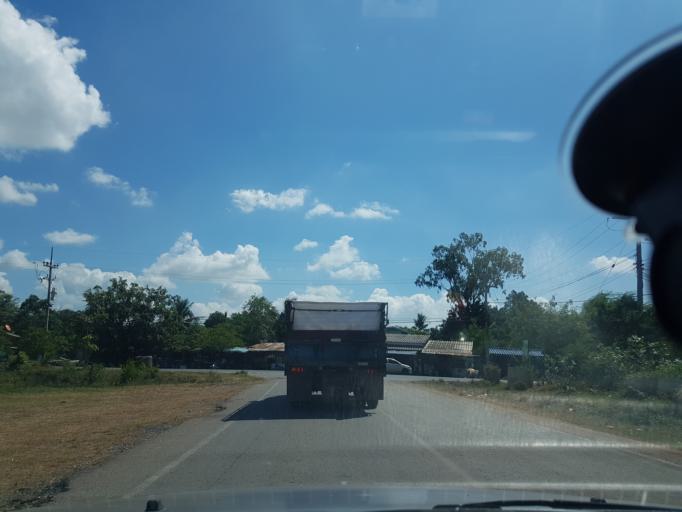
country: TH
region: Lop Buri
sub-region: Amphoe Tha Luang
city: Tha Luang
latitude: 14.9868
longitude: 101.0135
